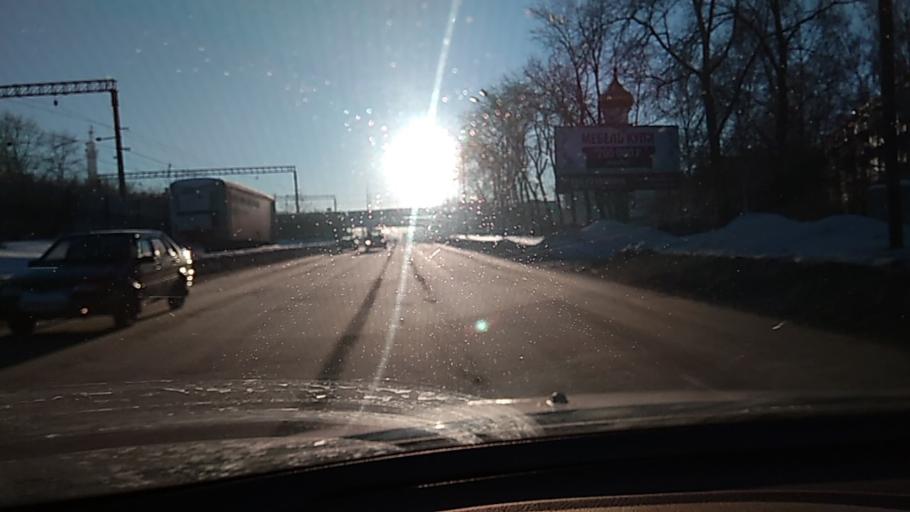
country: RU
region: Sverdlovsk
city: Yekaterinburg
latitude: 56.8511
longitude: 60.6231
